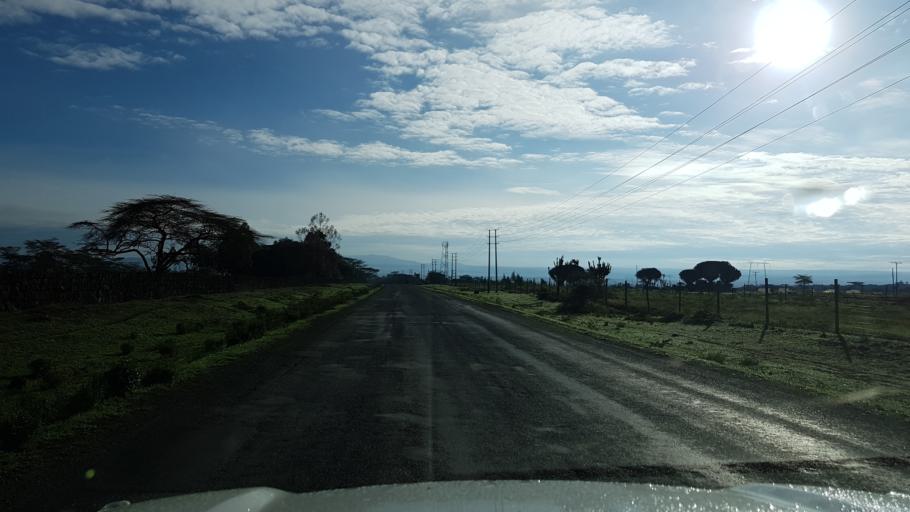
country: KE
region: Nakuru
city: Naivasha
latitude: -0.8180
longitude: 36.3918
